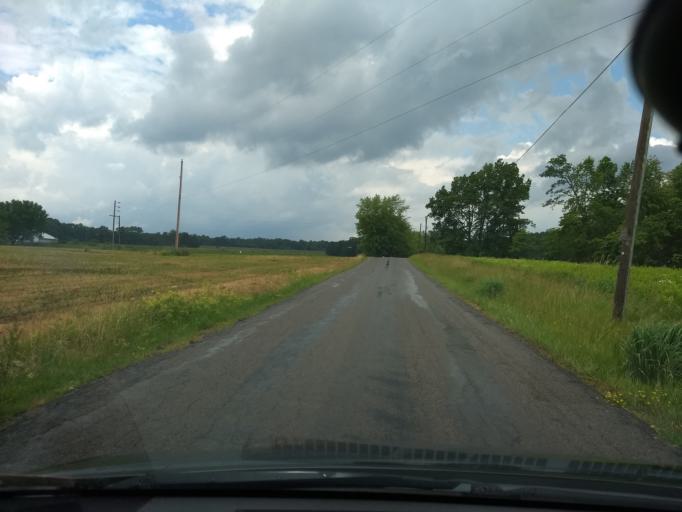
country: US
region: Pennsylvania
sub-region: Westmoreland County
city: Avonmore
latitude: 40.5436
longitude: -79.4983
